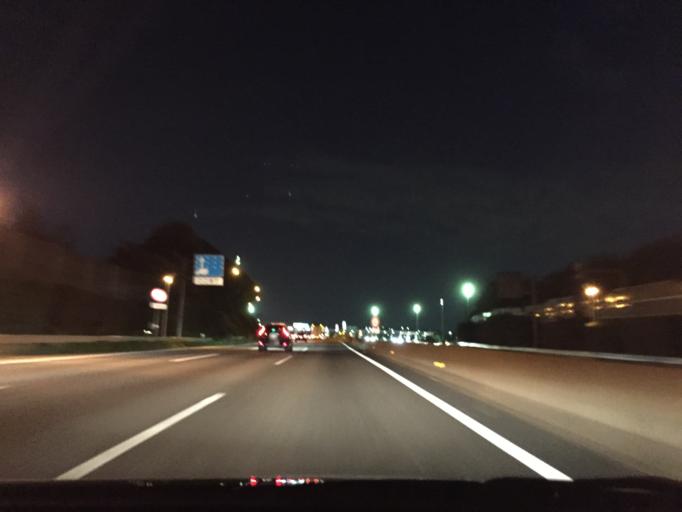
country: JP
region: Tokyo
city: Chofugaoka
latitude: 35.5967
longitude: 139.5764
